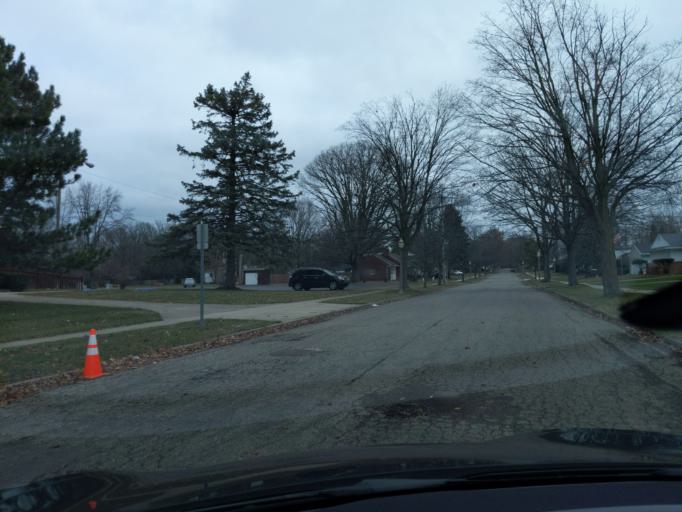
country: US
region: Michigan
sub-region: Ingham County
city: Edgemont Park
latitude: 42.7112
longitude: -84.5897
